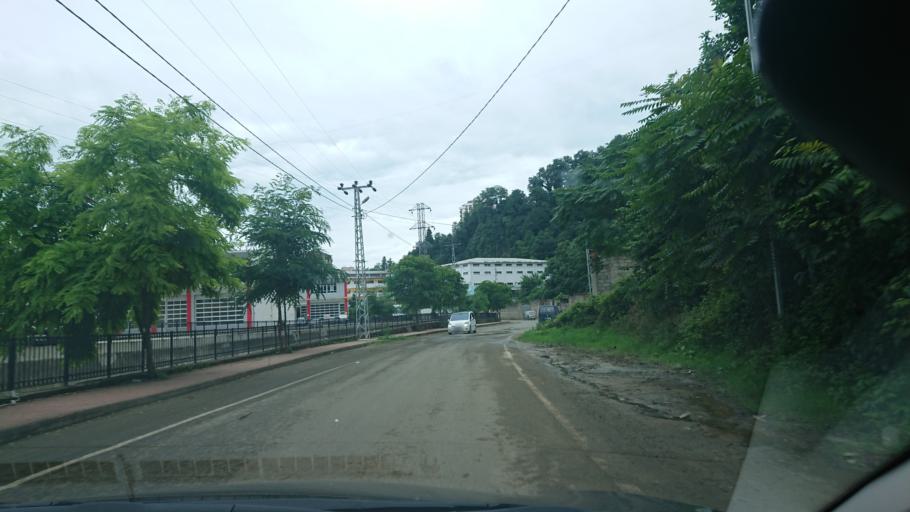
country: TR
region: Rize
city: Rize
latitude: 41.0305
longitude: 40.4829
